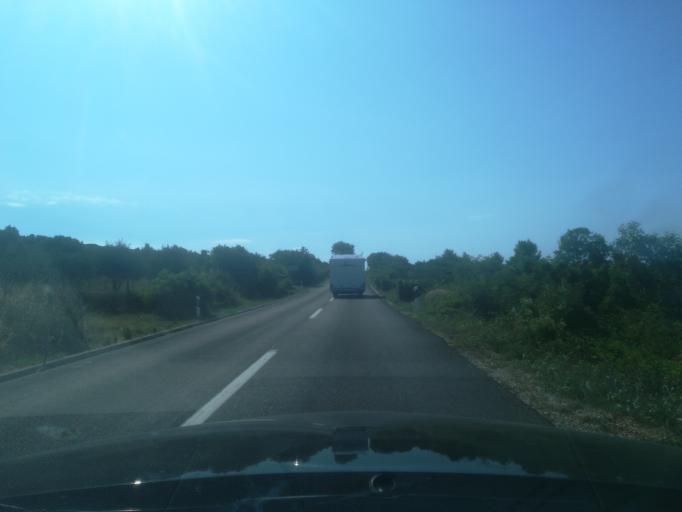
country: HR
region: Primorsko-Goranska
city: Banjol
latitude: 44.7243
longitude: 14.8193
